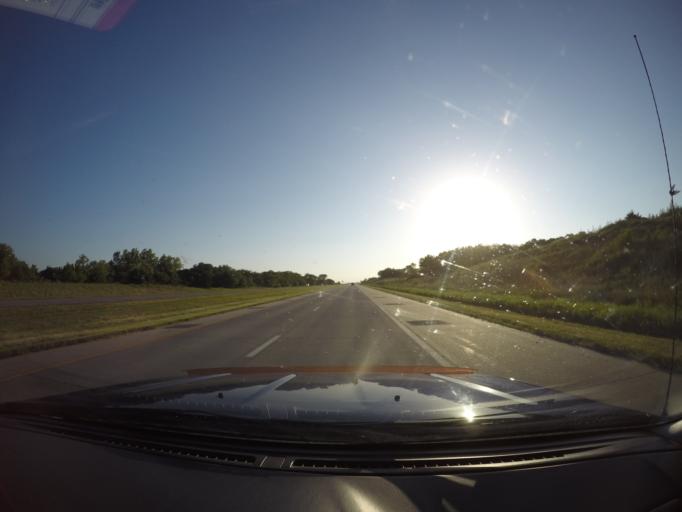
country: US
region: Kansas
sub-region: Riley County
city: Manhattan
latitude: 39.1982
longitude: -96.4670
